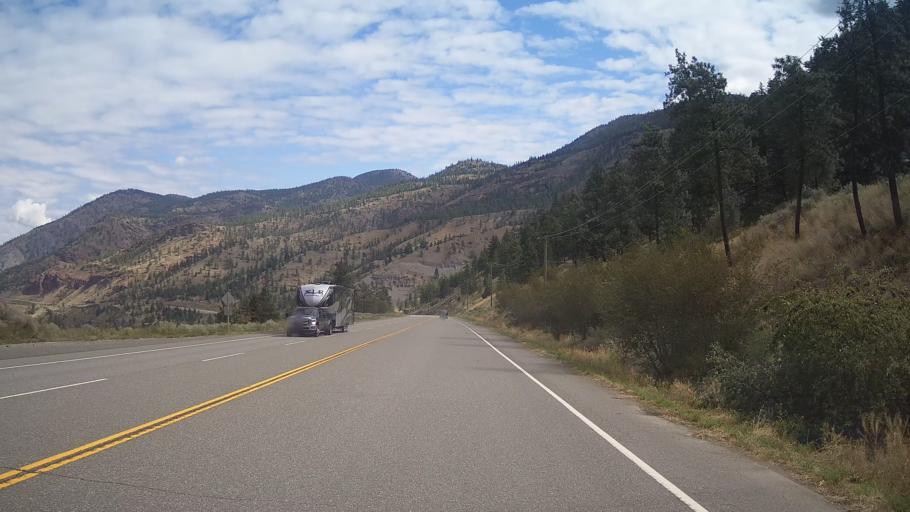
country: CA
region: British Columbia
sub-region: Thompson-Nicola Regional District
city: Ashcroft
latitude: 50.2882
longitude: -121.3990
